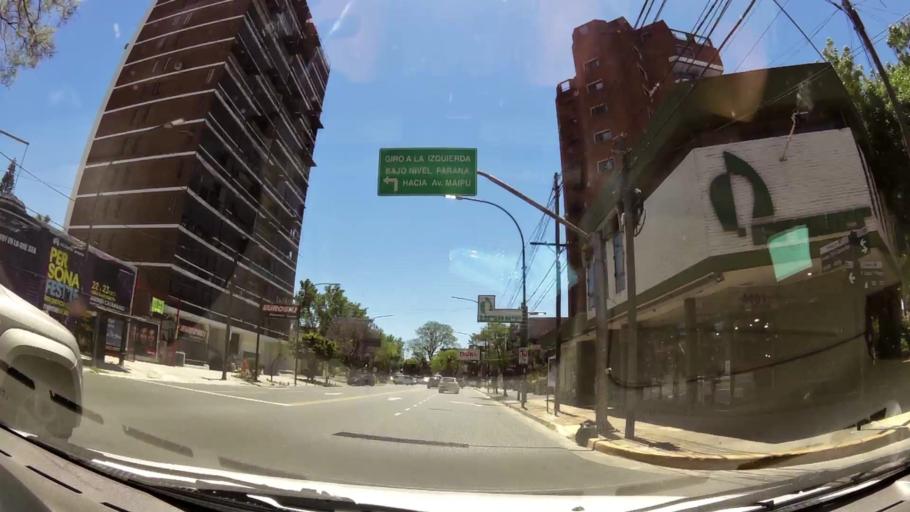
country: AR
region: Buenos Aires
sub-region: Partido de Vicente Lopez
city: Olivos
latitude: -34.4926
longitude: -58.4845
